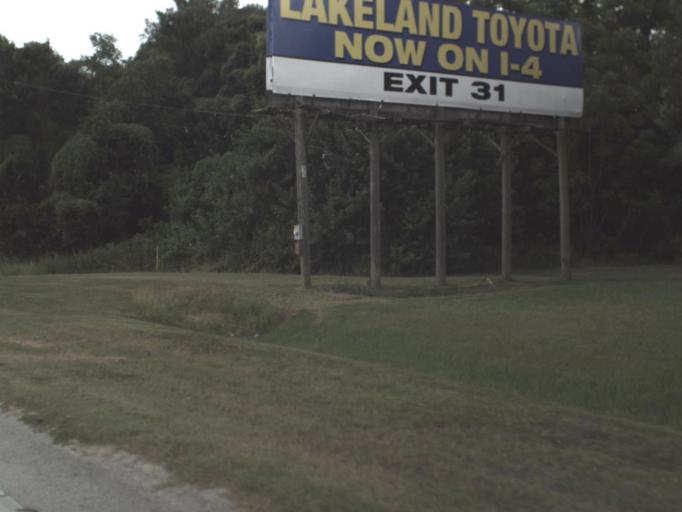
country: US
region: Florida
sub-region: Polk County
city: Mulberry
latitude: 27.8950
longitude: -81.9780
